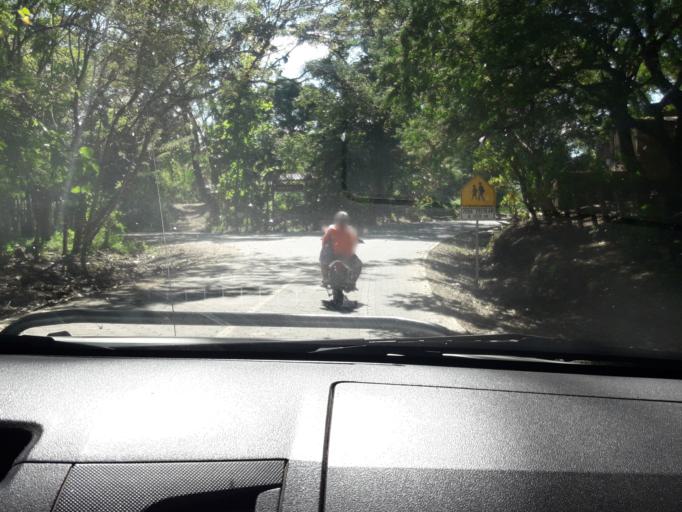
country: NI
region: Rivas
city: Cardenas
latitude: 11.2328
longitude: -85.6489
